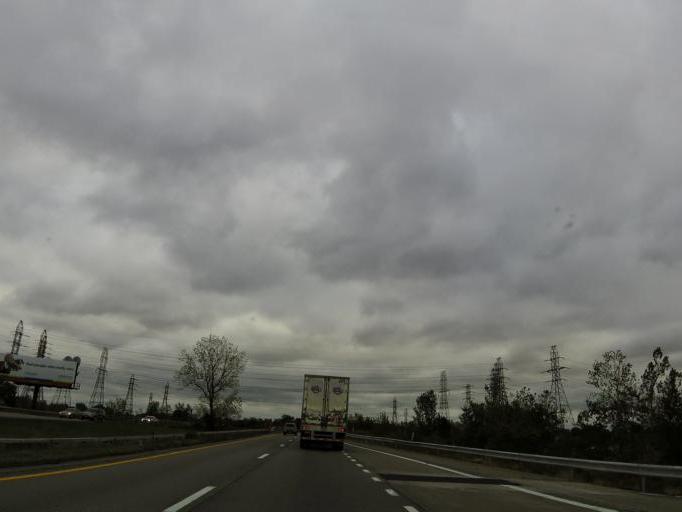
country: US
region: New York
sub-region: Erie County
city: West Seneca
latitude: 42.8458
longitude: -78.7762
